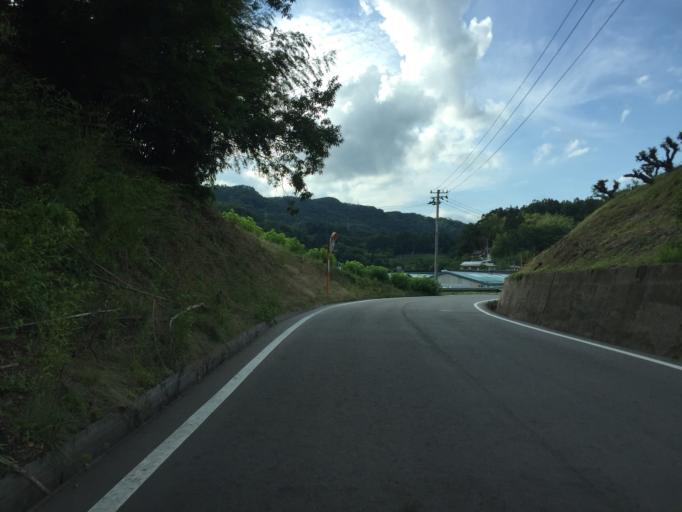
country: JP
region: Fukushima
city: Fukushima-shi
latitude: 37.6922
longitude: 140.5610
